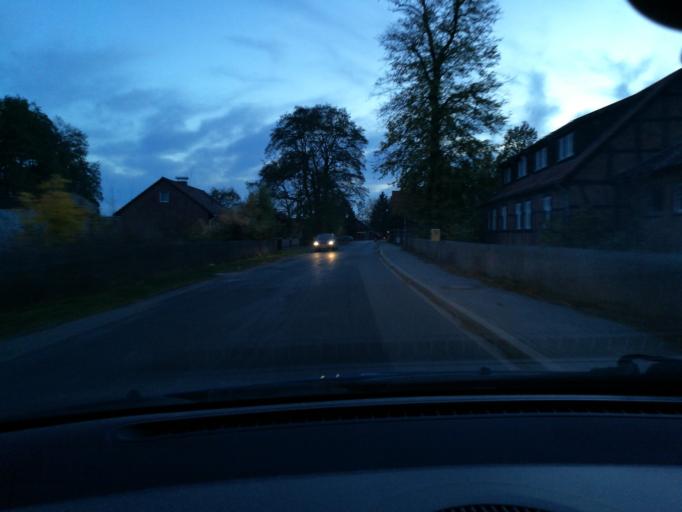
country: DE
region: Lower Saxony
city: Gartow
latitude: 53.0578
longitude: 11.4550
